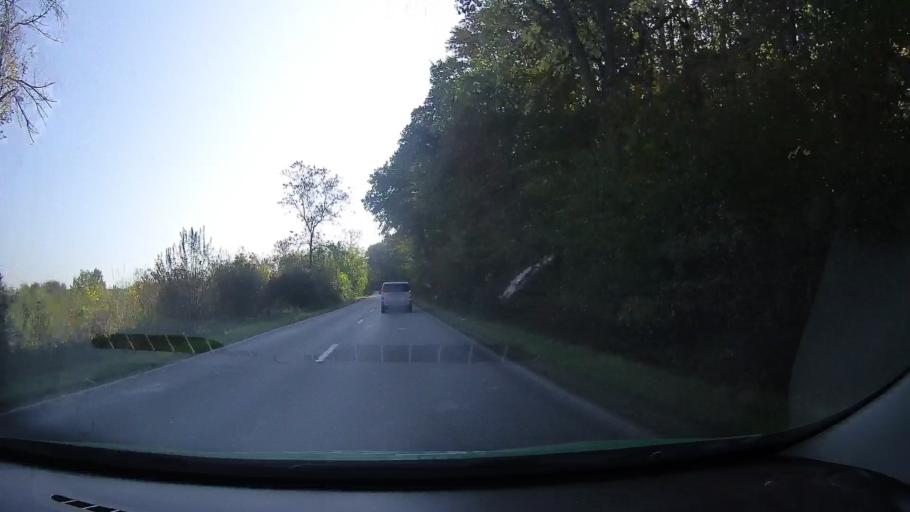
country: RO
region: Hunedoara
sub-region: Comuna Dobra
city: Dobra
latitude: 45.9112
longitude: 22.5217
